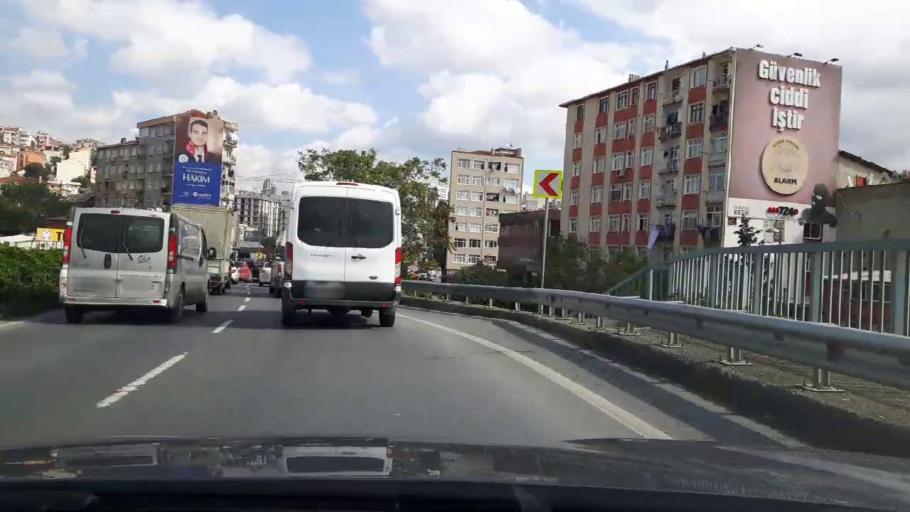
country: TR
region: Istanbul
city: Eminoenue
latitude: 41.0381
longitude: 28.9710
